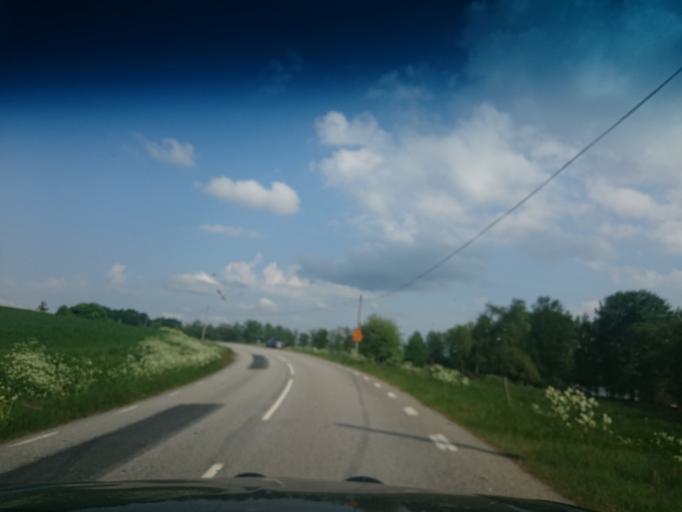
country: SE
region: Joenkoeping
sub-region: Vetlanda Kommun
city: Vetlanda
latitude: 57.3215
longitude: 15.0915
